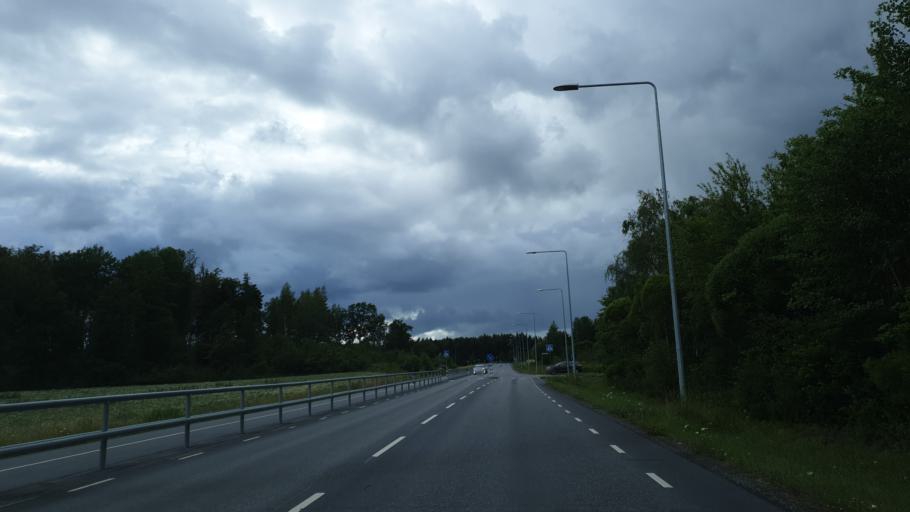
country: SE
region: Stockholm
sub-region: Jarfalla Kommun
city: Jakobsberg
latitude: 59.4219
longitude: 17.8080
